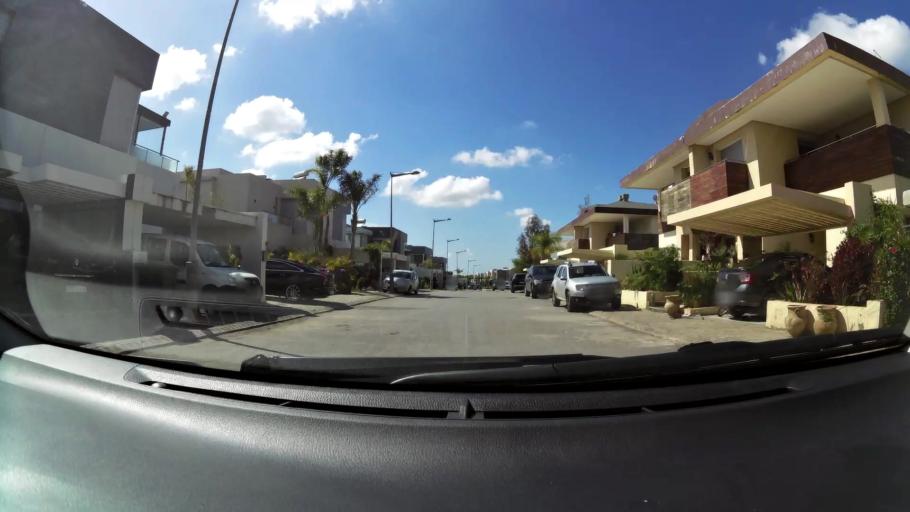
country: MA
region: Grand Casablanca
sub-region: Nouaceur
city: Bouskoura
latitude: 33.4652
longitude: -7.6031
